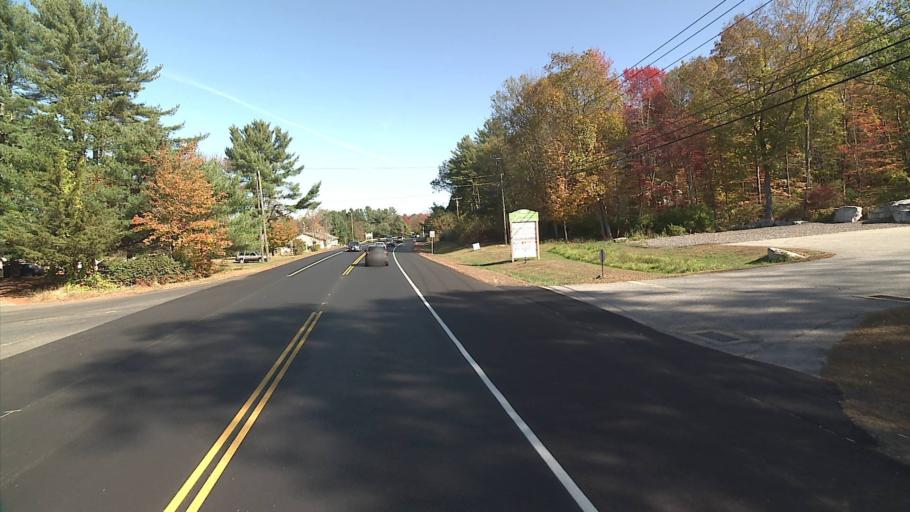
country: US
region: Connecticut
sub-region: Windham County
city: Windham
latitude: 41.7549
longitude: -72.1493
